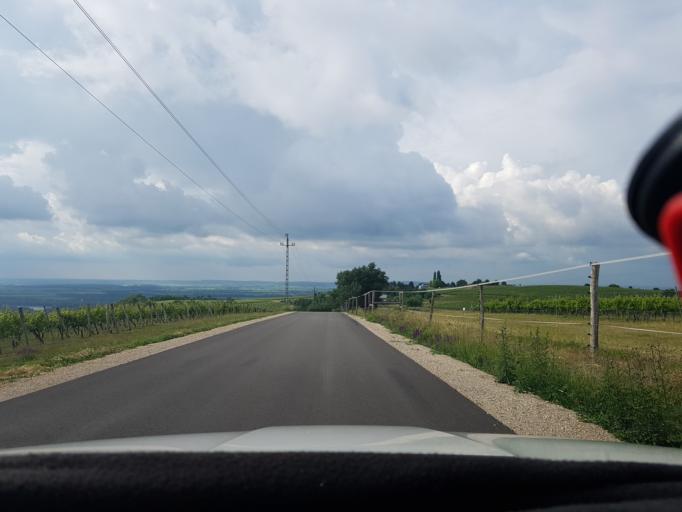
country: HU
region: Komarom-Esztergom
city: Neszmely
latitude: 47.7192
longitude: 18.3786
